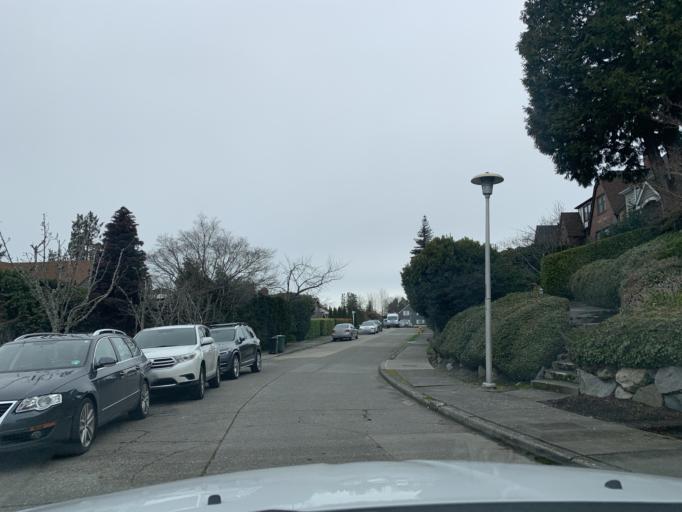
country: US
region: Washington
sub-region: King County
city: Medina
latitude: 47.6563
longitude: -122.2787
